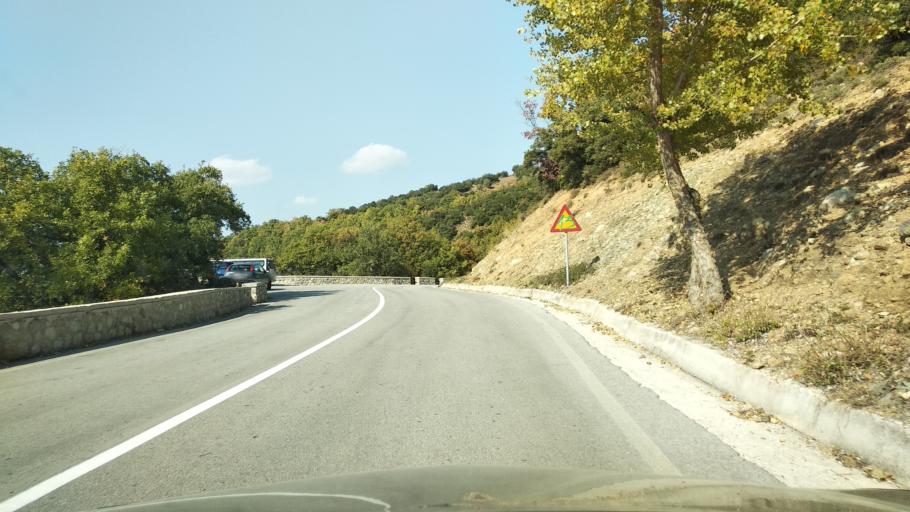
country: GR
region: Thessaly
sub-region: Trikala
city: Kalampaka
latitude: 39.7189
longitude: 21.6375
